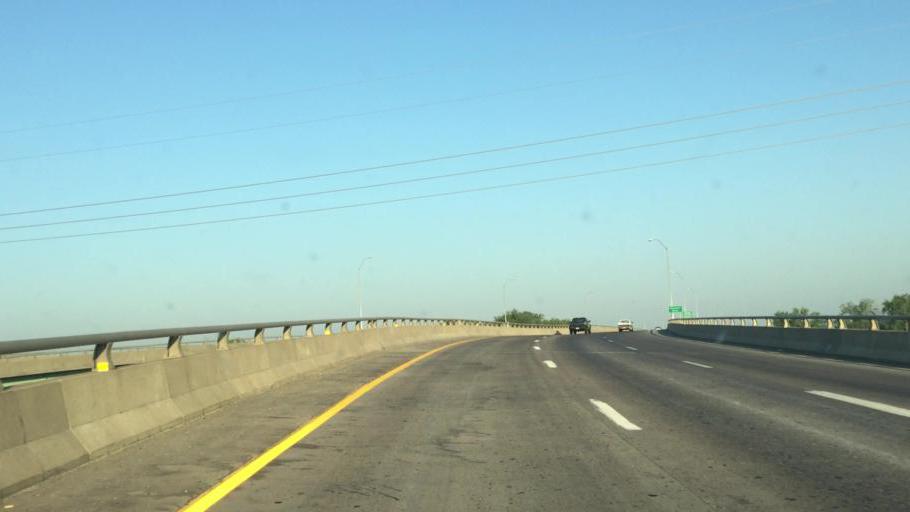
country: US
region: Kansas
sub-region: Doniphan County
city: Elwood
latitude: 39.7486
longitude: -94.8565
